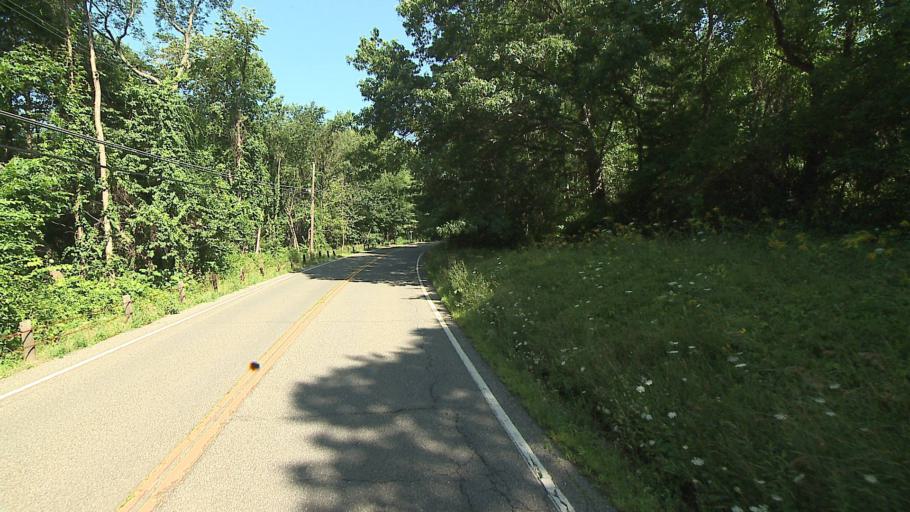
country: US
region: Connecticut
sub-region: Litchfield County
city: Canaan
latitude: 42.0134
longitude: -73.4287
